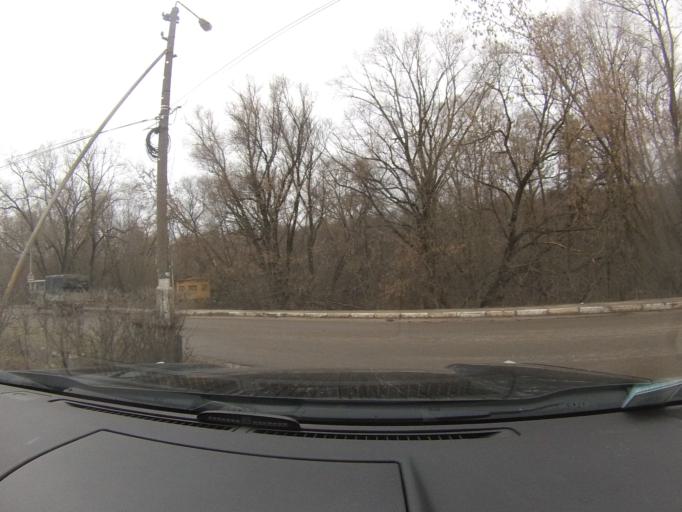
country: RU
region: Moskovskaya
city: Peski
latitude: 55.2609
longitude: 38.7636
